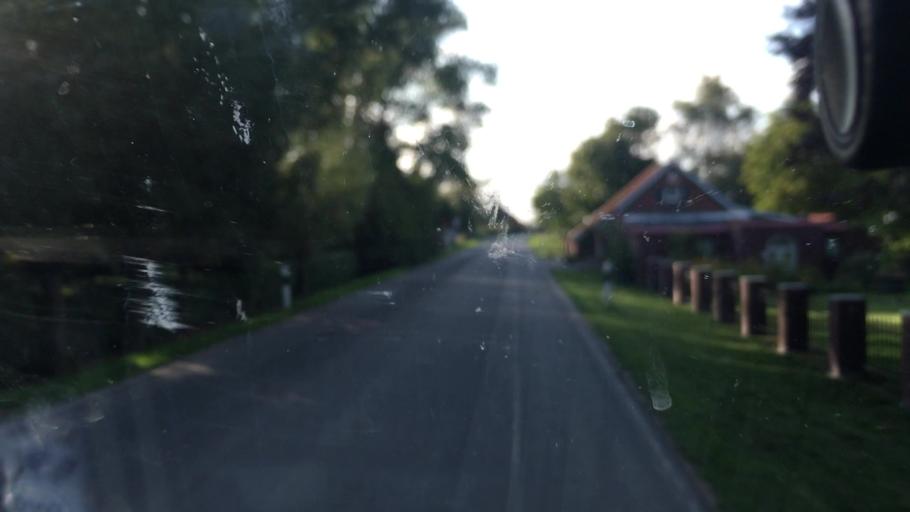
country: DE
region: Lower Saxony
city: Werdum
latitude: 53.6552
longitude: 7.7790
